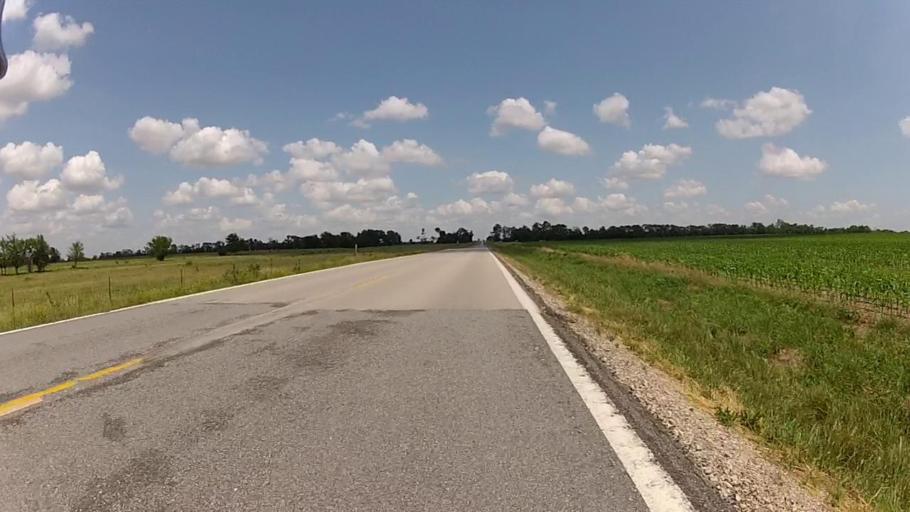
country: US
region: Kansas
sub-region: Labette County
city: Altamont
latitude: 37.1926
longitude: -95.3720
